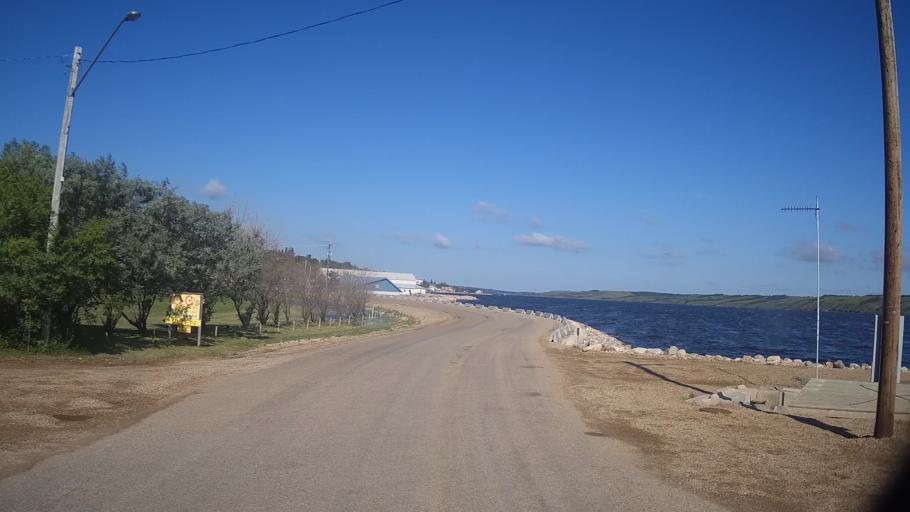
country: CA
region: Saskatchewan
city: Watrous
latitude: 51.7188
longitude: -105.4293
